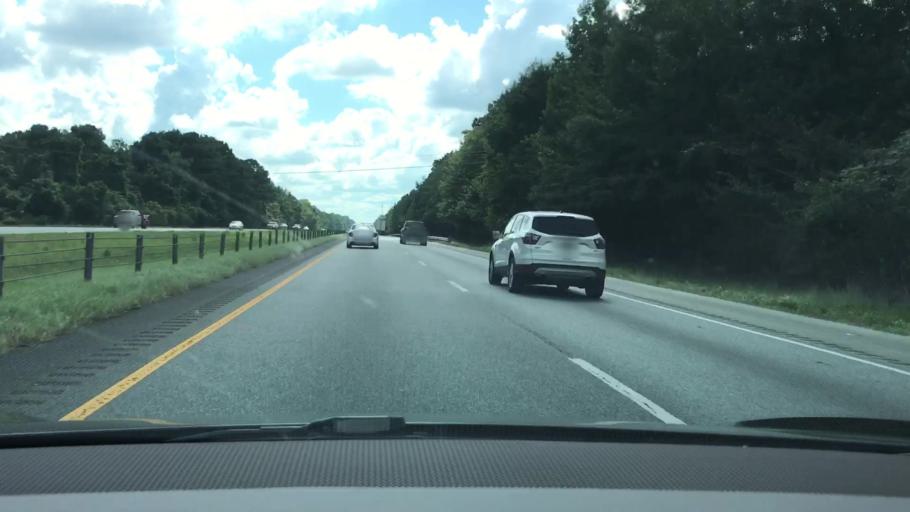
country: US
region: Alabama
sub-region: Lee County
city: Auburn
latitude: 32.5783
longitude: -85.4730
